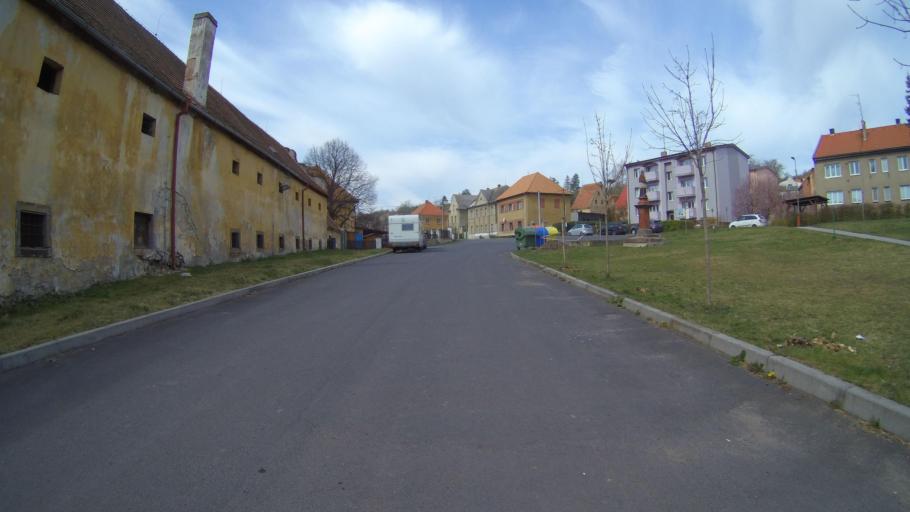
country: CZ
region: Ustecky
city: Mecholupy
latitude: 50.2541
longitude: 13.5146
